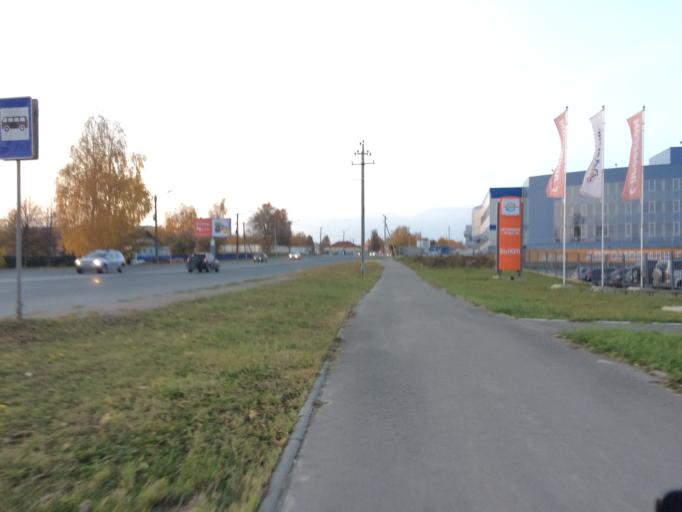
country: RU
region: Mariy-El
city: Yoshkar-Ola
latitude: 56.6047
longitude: 47.8815
